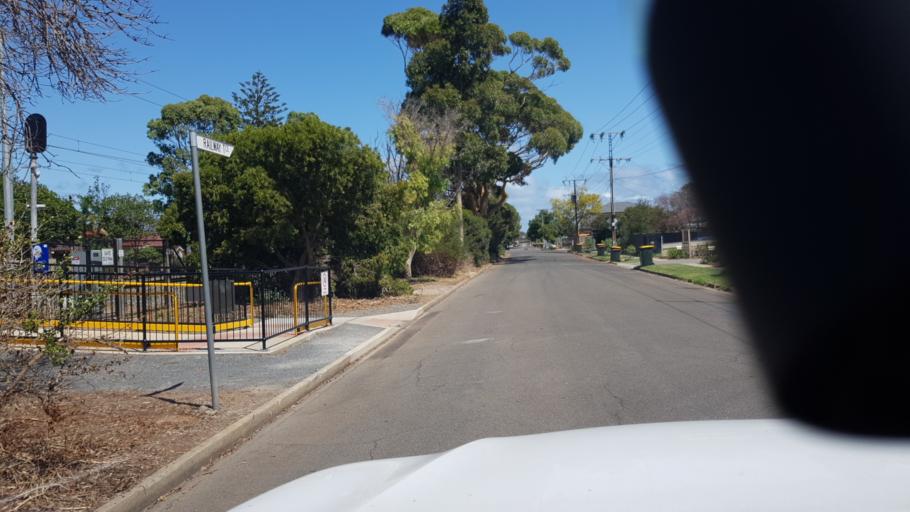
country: AU
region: South Australia
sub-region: Adelaide
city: Brighton
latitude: -35.0113
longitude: 138.5317
